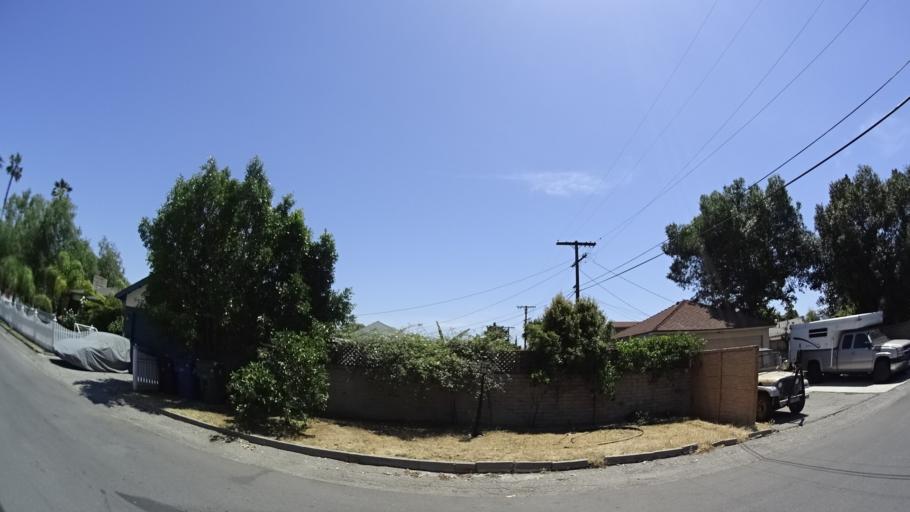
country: US
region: California
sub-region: Los Angeles County
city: North Hollywood
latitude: 34.1849
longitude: -118.3773
